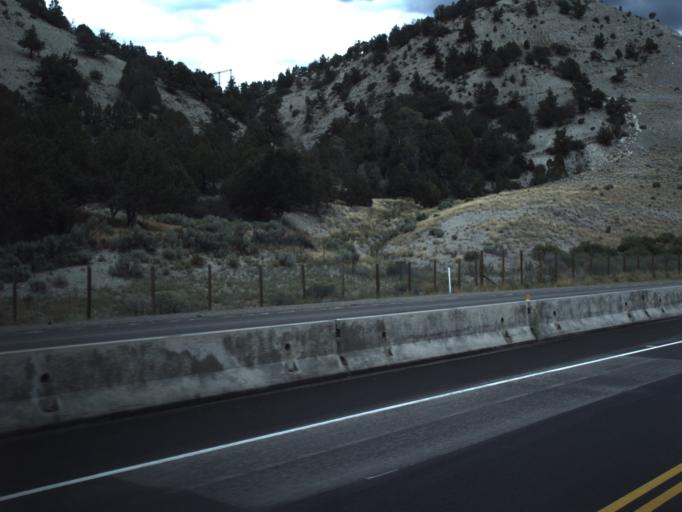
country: US
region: Utah
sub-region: Utah County
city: Mapleton
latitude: 39.9569
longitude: -111.2485
